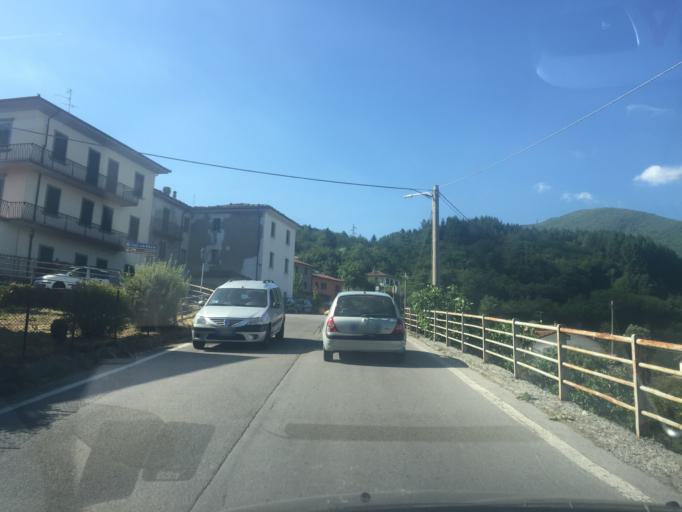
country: IT
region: Tuscany
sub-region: Provincia di Lucca
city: San Romano in Garfagnana
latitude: 44.1471
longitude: 10.3531
